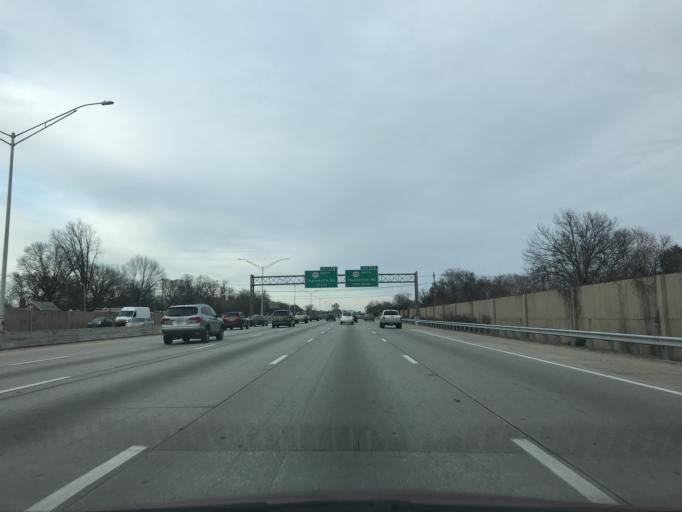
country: US
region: Kentucky
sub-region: Jefferson County
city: West Buechel
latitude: 38.2145
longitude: -85.6643
